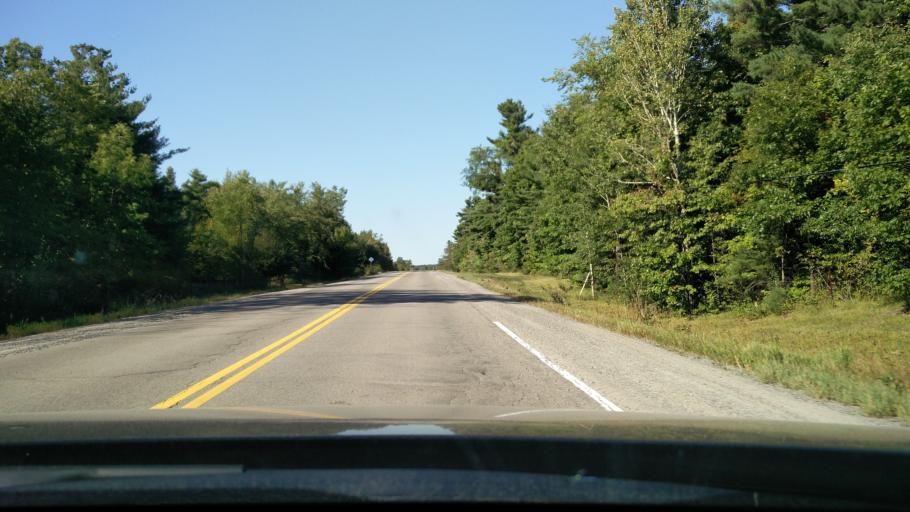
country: CA
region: Ontario
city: Perth
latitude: 44.7184
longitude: -76.4012
